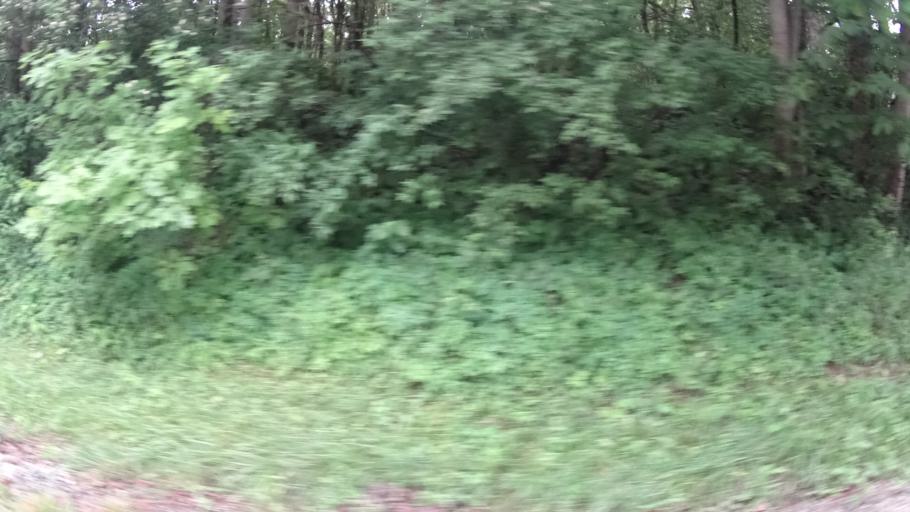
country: US
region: Ohio
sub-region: Erie County
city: Milan
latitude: 41.3381
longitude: -82.5669
